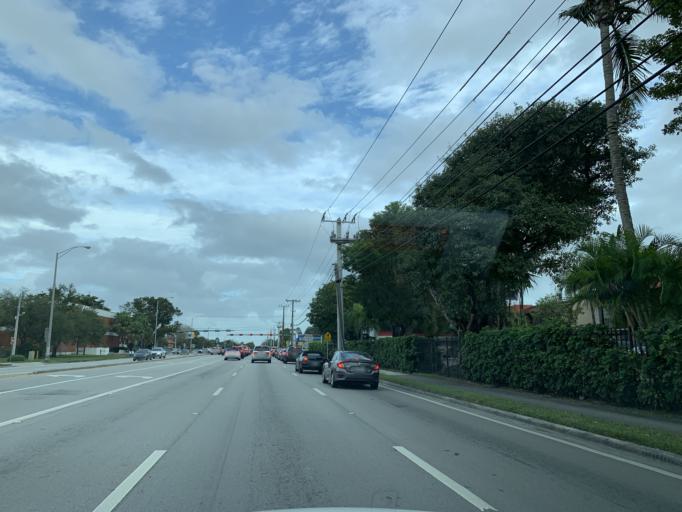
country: US
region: Florida
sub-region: Miami-Dade County
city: Sunset
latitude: 25.6869
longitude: -80.3676
